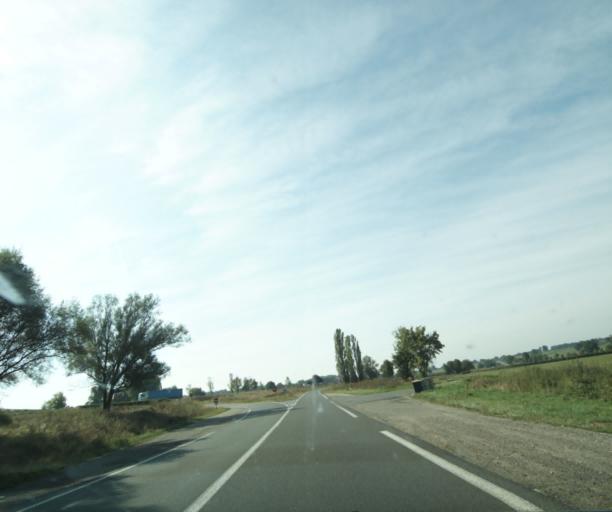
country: FR
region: Bourgogne
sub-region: Departement de Saone-et-Loire
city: Genelard
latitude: 46.5937
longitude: 4.2305
